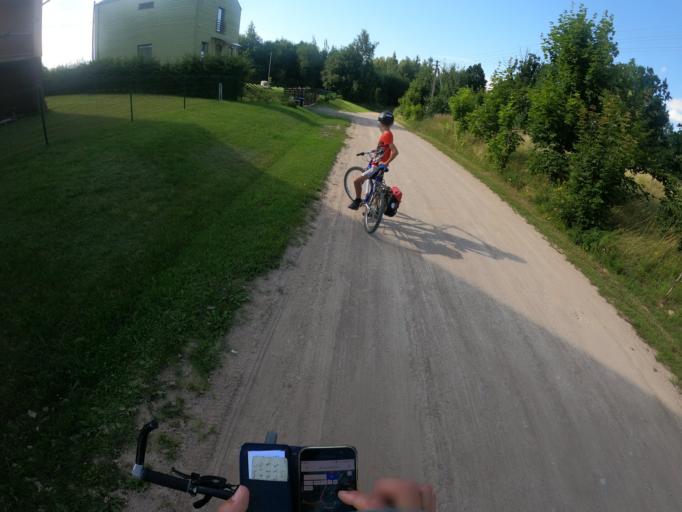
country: LT
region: Telsiu apskritis
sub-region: Telsiai
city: Telsiai
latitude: 55.9689
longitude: 22.2021
